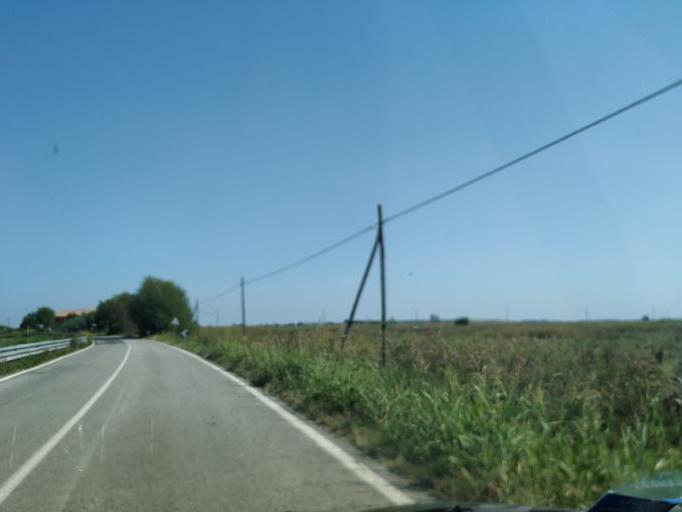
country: IT
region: Emilia-Romagna
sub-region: Provincia di Ferrara
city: Formignana
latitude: 44.8763
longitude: 11.8890
